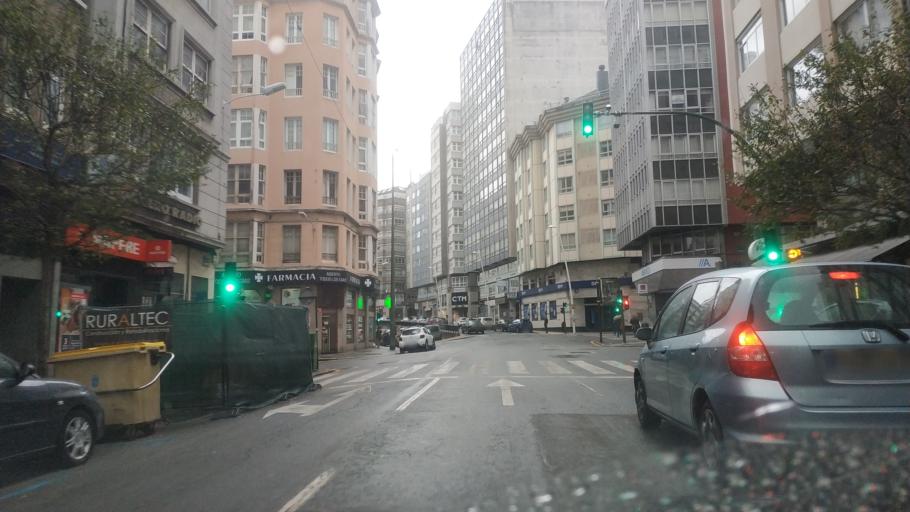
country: ES
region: Galicia
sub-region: Provincia da Coruna
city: A Coruna
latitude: 43.3625
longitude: -8.4081
